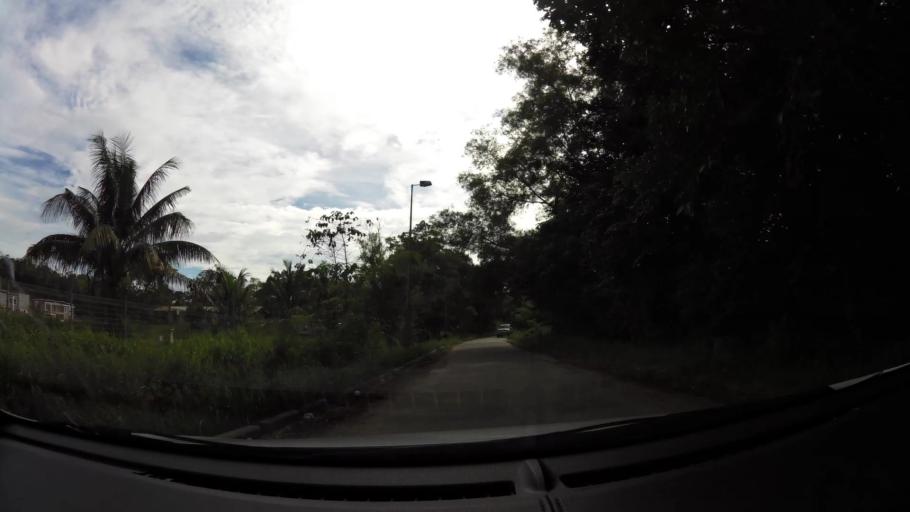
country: BN
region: Brunei and Muara
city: Bandar Seri Begawan
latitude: 4.8962
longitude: 114.8910
